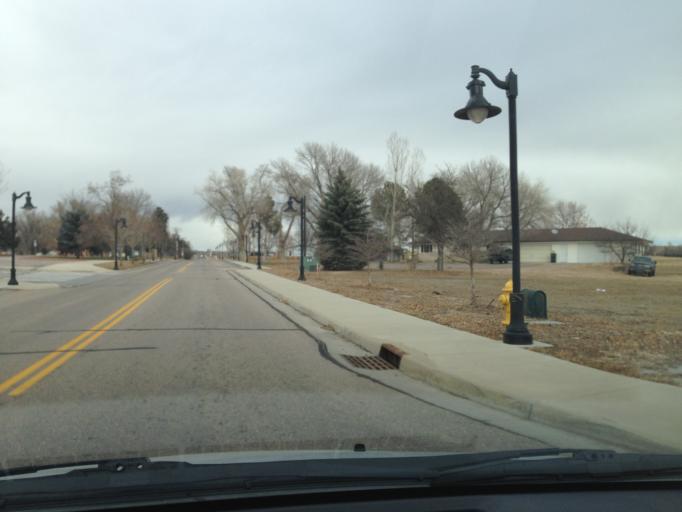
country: US
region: Colorado
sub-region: Weld County
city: Windsor
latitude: 40.5315
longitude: -104.9823
